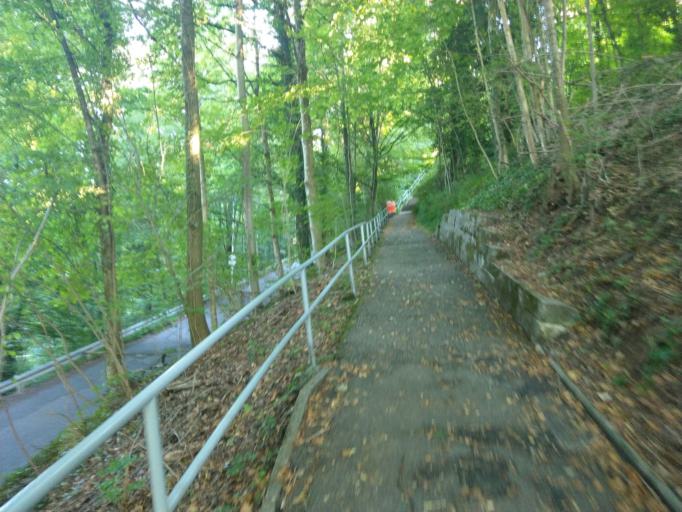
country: DE
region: Baden-Wuerttemberg
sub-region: Tuebingen Region
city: Ravensburg
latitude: 47.7754
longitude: 9.6166
